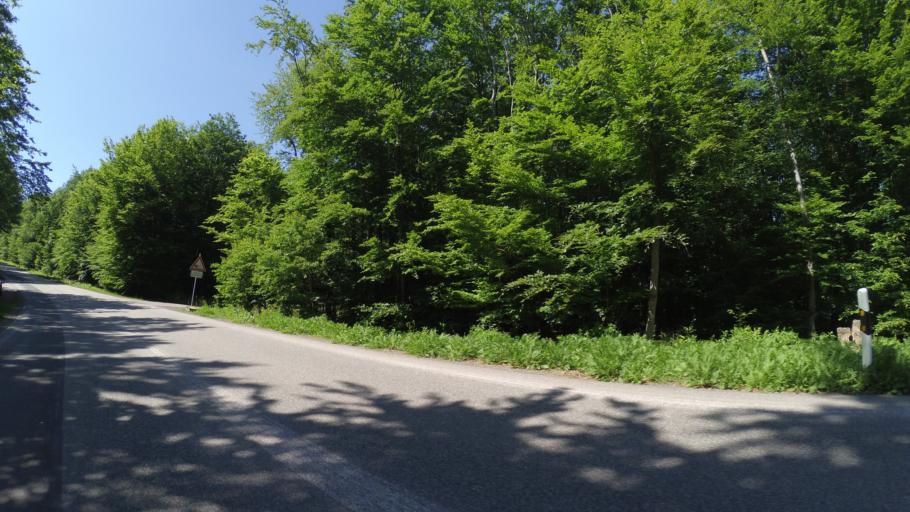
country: DE
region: Saarland
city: Quierschied
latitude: 49.3102
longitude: 7.0130
